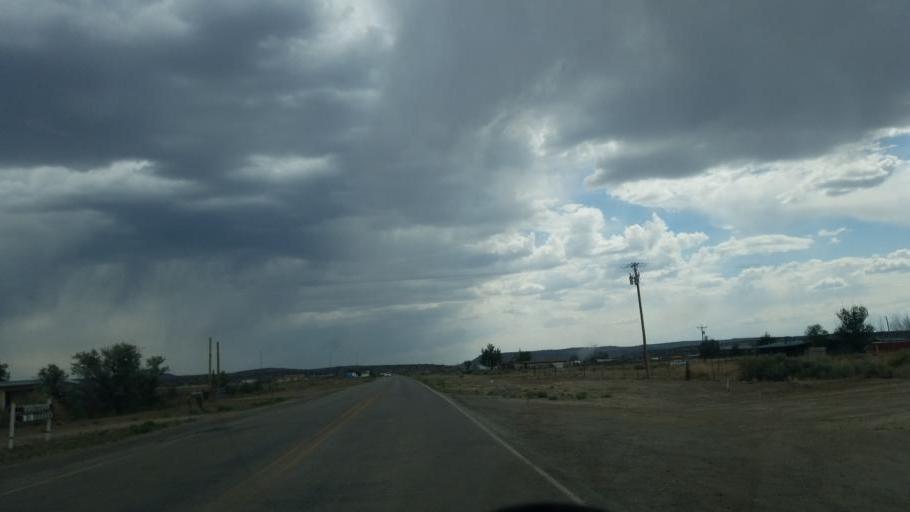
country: US
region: New Mexico
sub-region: McKinley County
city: Gallup
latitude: 35.4907
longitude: -108.8958
